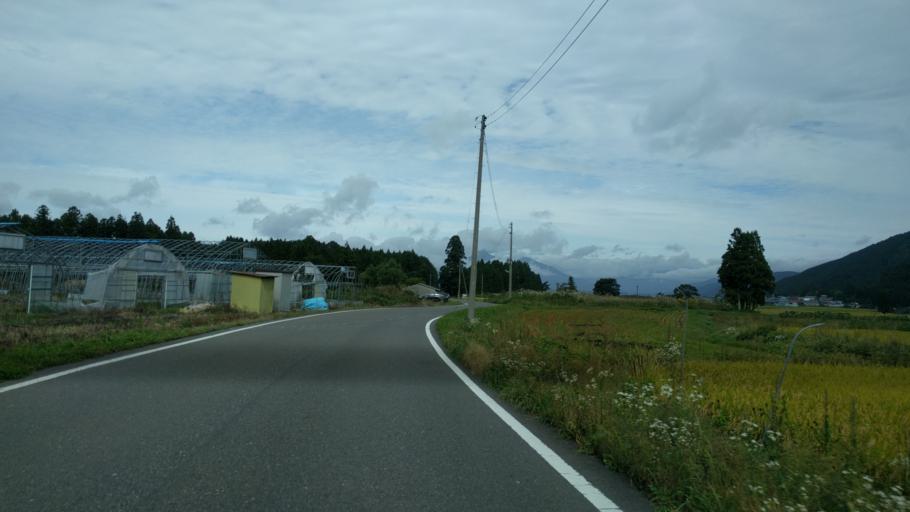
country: JP
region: Fukushima
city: Inawashiro
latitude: 37.4085
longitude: 140.1450
